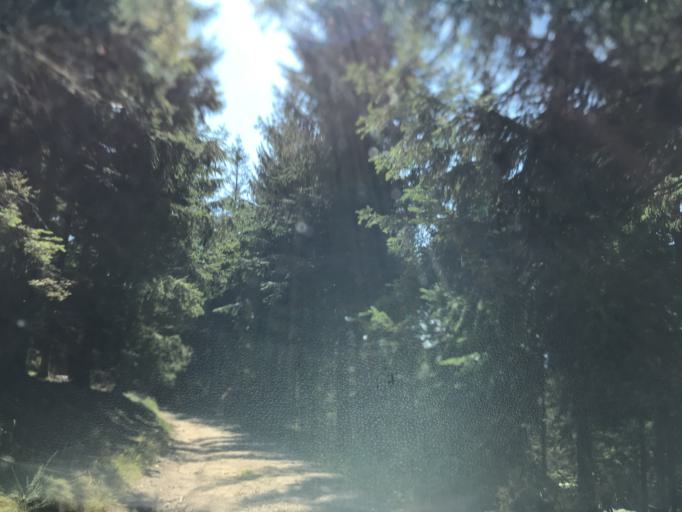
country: FR
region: Rhone-Alpes
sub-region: Departement de la Loire
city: Noiretable
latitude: 45.7609
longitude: 3.7552
